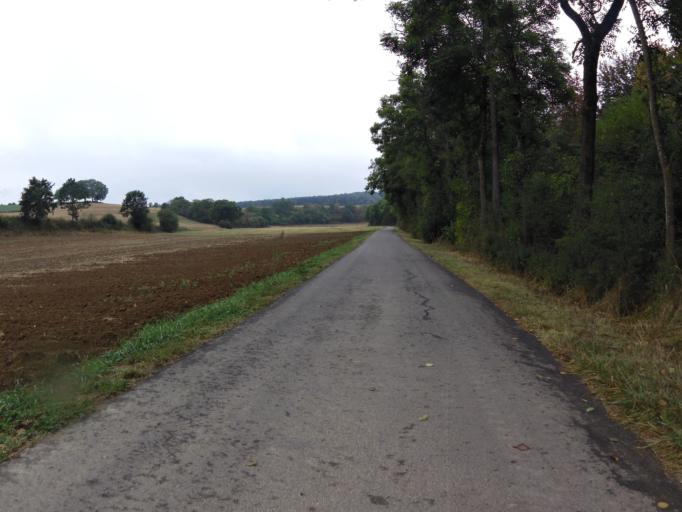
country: DE
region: Bavaria
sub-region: Regierungsbezirk Unterfranken
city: Gadheim
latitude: 49.8497
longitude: 9.9136
